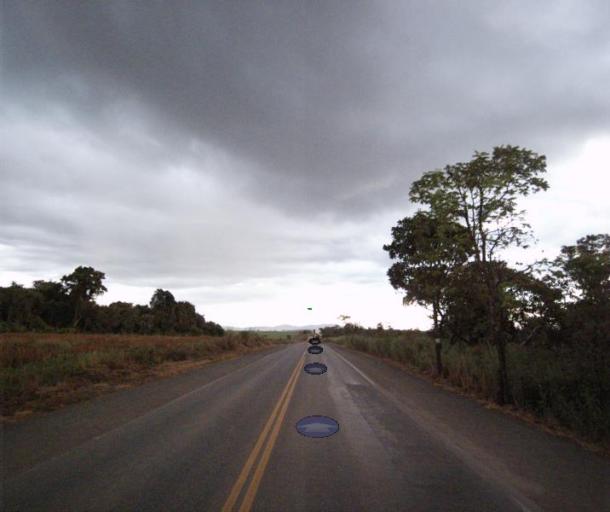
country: BR
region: Goias
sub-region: Uruacu
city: Uruacu
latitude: -14.6624
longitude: -49.1940
